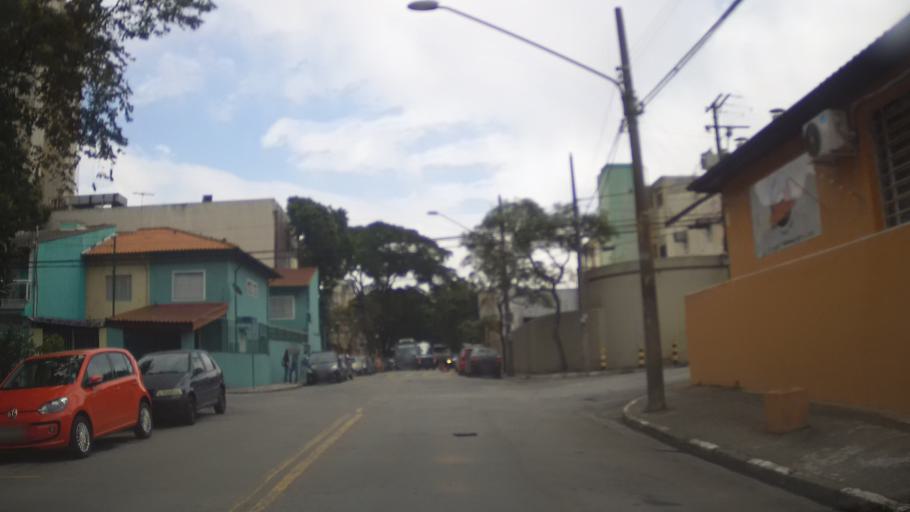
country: BR
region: Sao Paulo
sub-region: Guarulhos
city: Guarulhos
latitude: -23.4838
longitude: -46.5505
